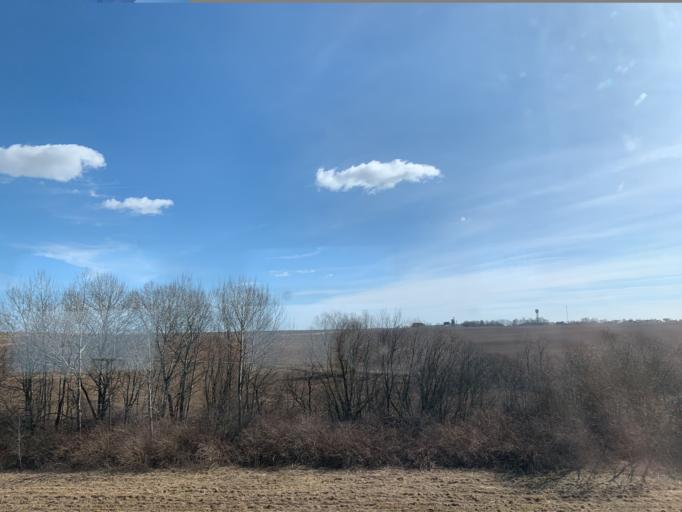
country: BY
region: Minsk
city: Haradzyeya
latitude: 53.3277
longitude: 26.5457
